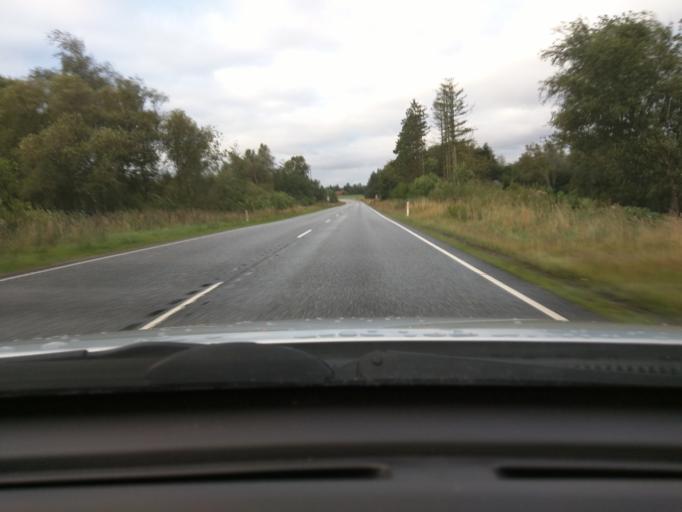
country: DK
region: Central Jutland
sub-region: Silkeborg Kommune
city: Kjellerup
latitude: 56.2726
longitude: 9.3172
